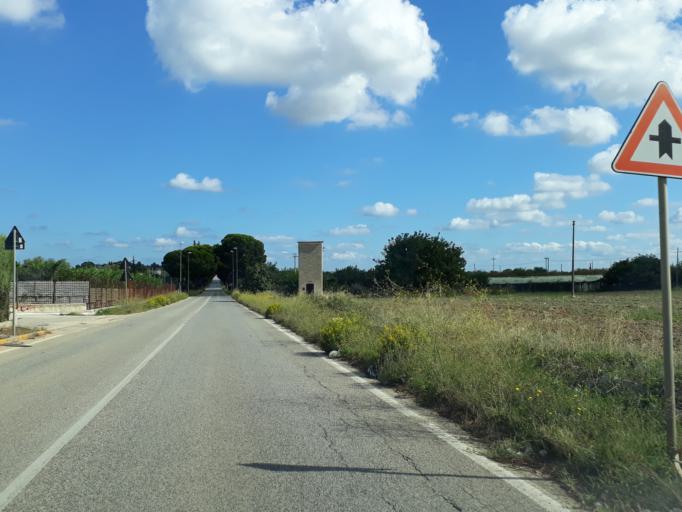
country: IT
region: Apulia
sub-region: Provincia di Bari
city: Rutigliano
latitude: 41.0188
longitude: 17.0222
